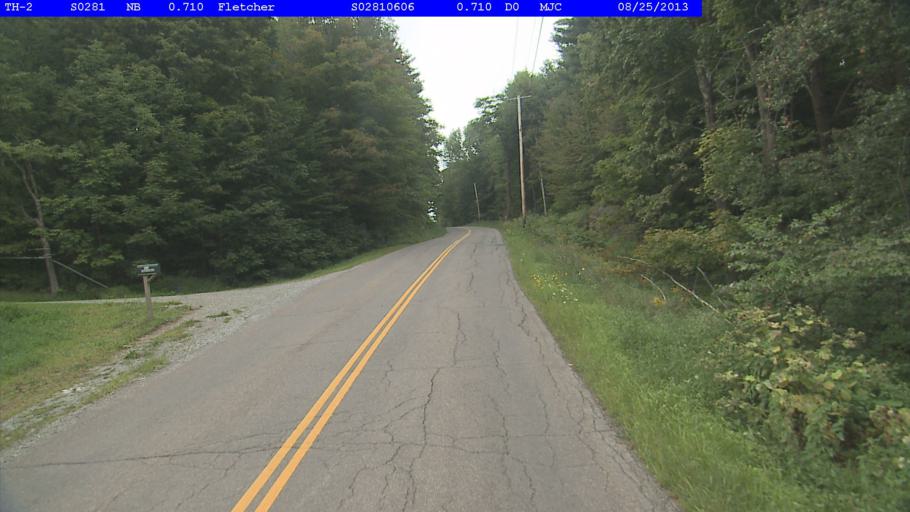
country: US
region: Vermont
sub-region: Chittenden County
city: Milton
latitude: 44.6891
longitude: -72.9255
